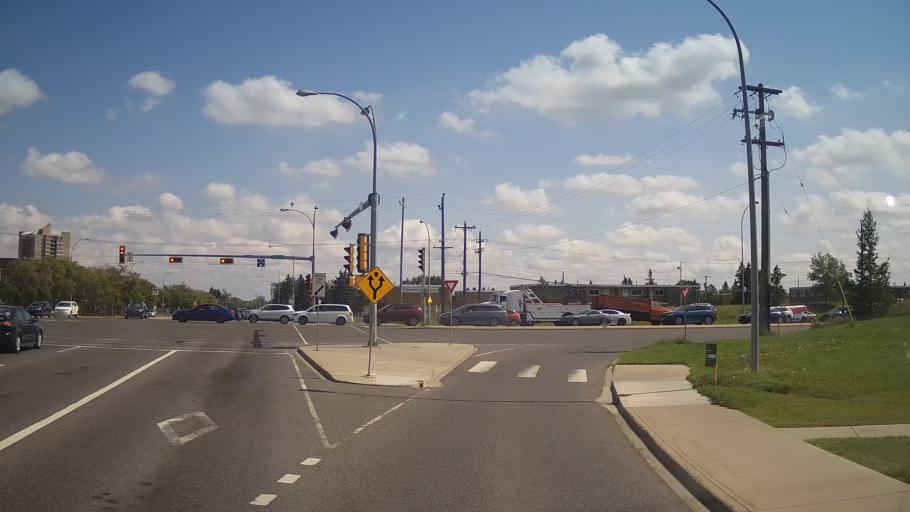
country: CA
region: Alberta
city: St. Albert
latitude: 53.5194
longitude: -113.6163
